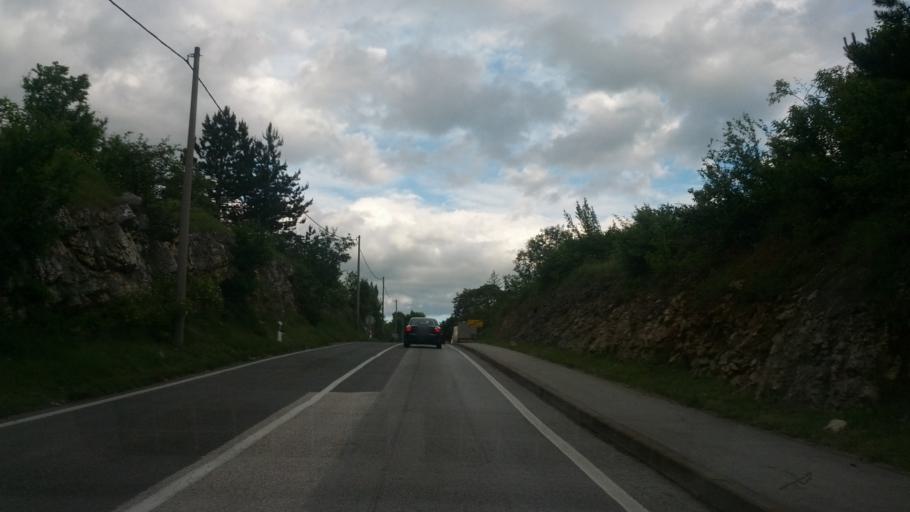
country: HR
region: Licko-Senjska
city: Jezerce
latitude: 44.9574
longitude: 15.6603
